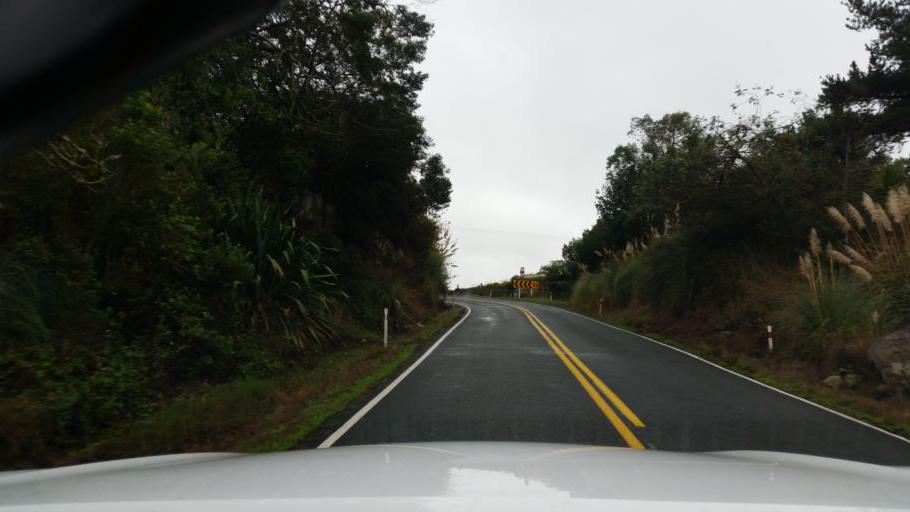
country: NZ
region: Northland
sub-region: Kaipara District
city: Dargaville
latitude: -36.0836
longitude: 173.9531
